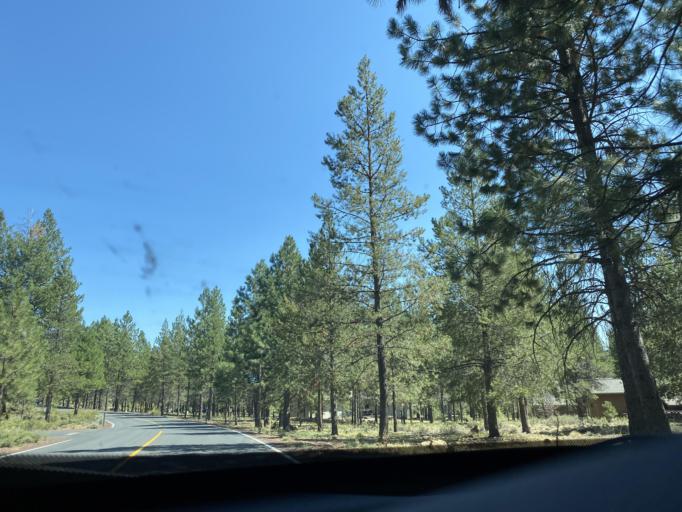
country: US
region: Oregon
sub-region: Deschutes County
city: Sunriver
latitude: 43.8895
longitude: -121.4361
